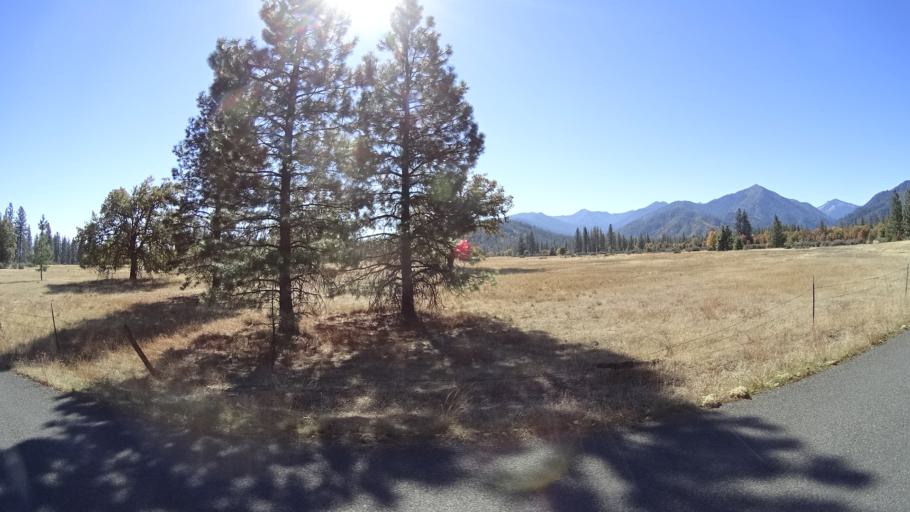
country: US
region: California
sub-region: Siskiyou County
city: Yreka
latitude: 41.5485
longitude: -122.9325
